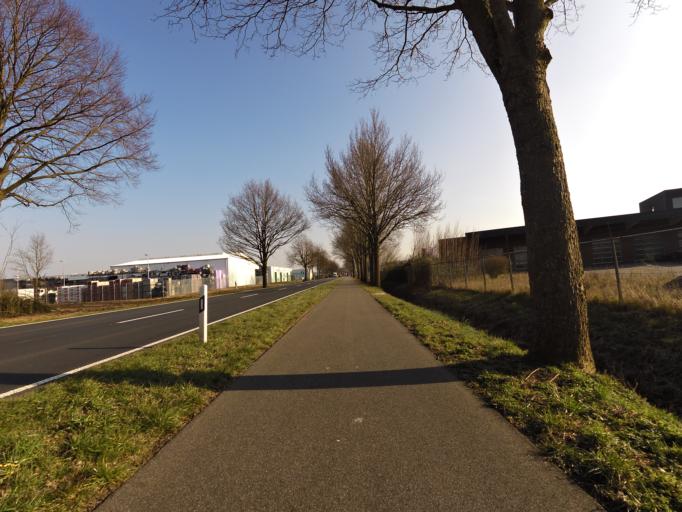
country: DE
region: North Rhine-Westphalia
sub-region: Regierungsbezirk Dusseldorf
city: Emmerich
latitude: 51.8460
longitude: 6.2704
